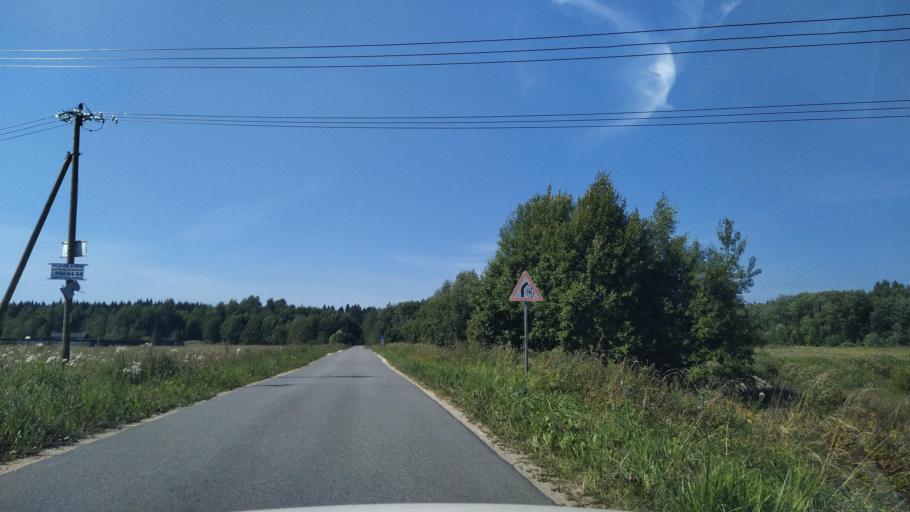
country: RU
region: Leningrad
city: Rozhdestveno
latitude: 59.2617
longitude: 30.0294
